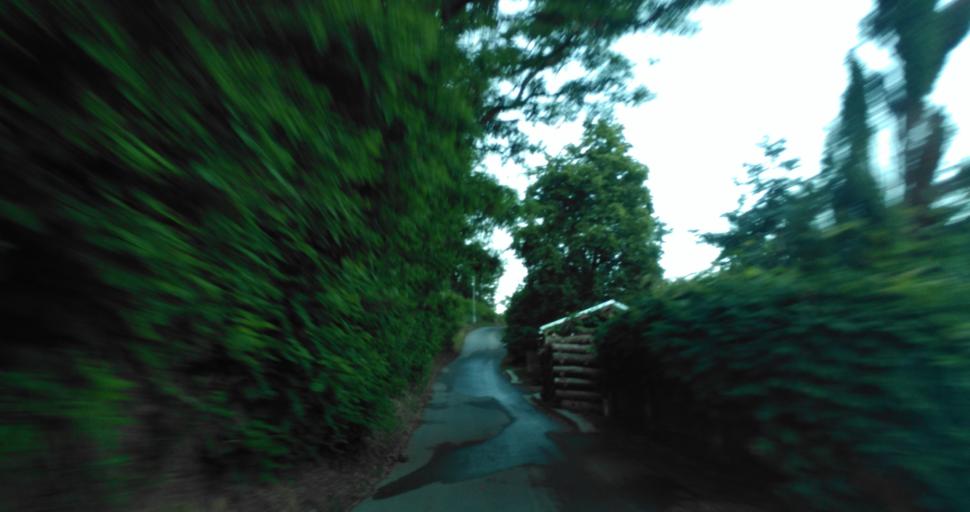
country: CZ
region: Central Bohemia
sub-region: Okres Beroun
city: Beroun
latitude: 49.9704
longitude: 14.0599
